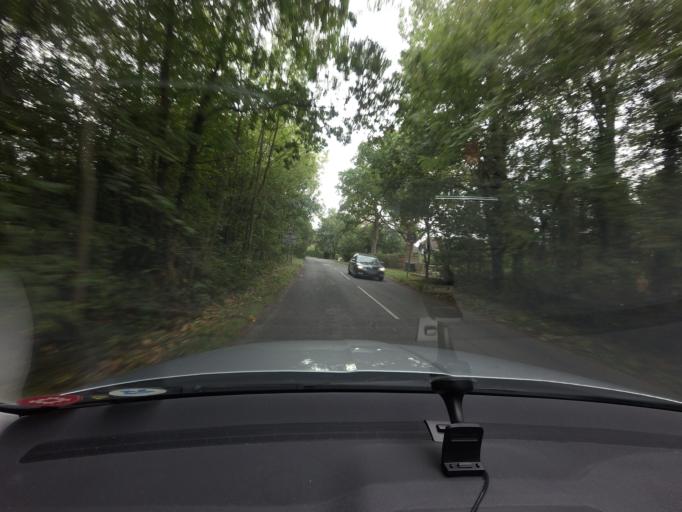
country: GB
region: England
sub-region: Kent
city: Borough Green
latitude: 51.2999
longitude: 0.2850
